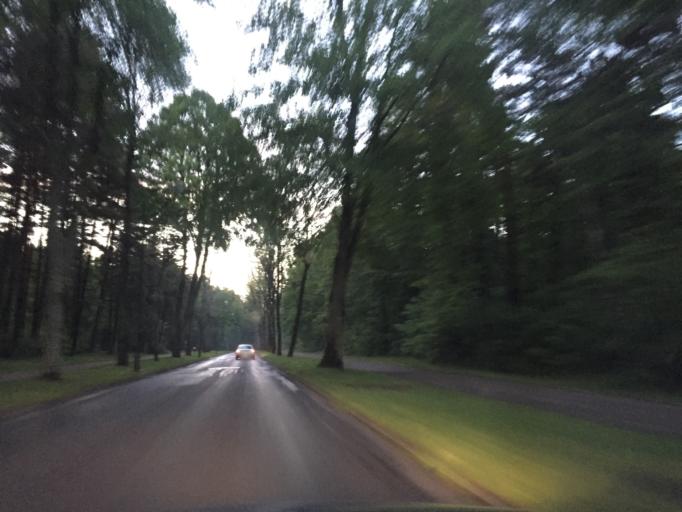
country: LT
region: Klaipedos apskritis
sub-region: Klaipeda
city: Palanga
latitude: 55.9006
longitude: 21.0617
